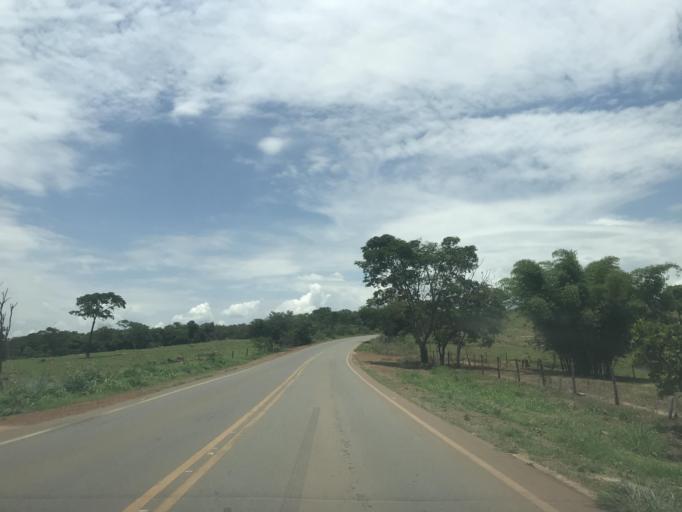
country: BR
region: Goias
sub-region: Vianopolis
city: Vianopolis
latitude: -16.7016
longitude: -48.3882
